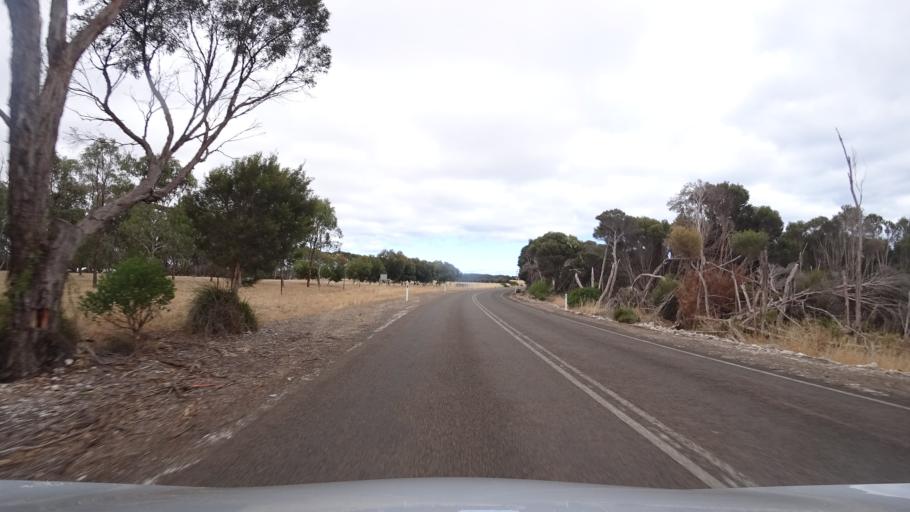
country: AU
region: South Australia
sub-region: Kangaroo Island
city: Kingscote
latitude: -35.6140
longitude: 137.5259
